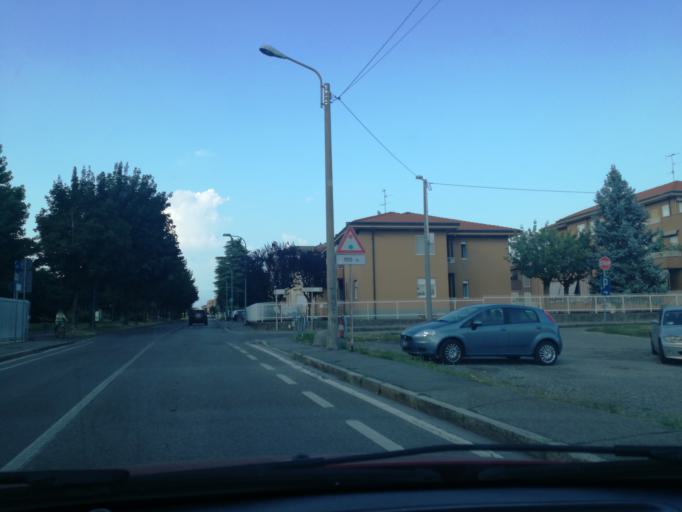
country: IT
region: Lombardy
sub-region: Provincia di Monza e Brianza
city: Arcore
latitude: 45.6319
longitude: 9.3295
